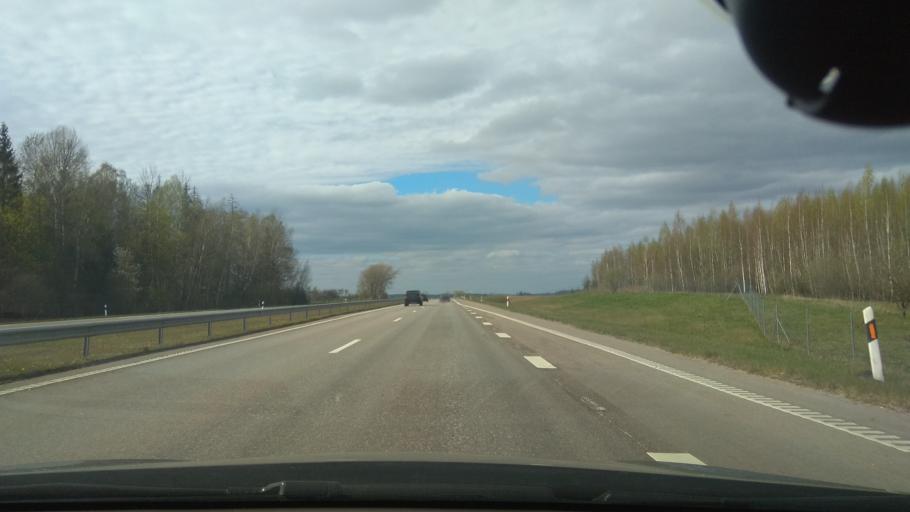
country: LT
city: Sirvintos
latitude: 55.1223
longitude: 24.8410
